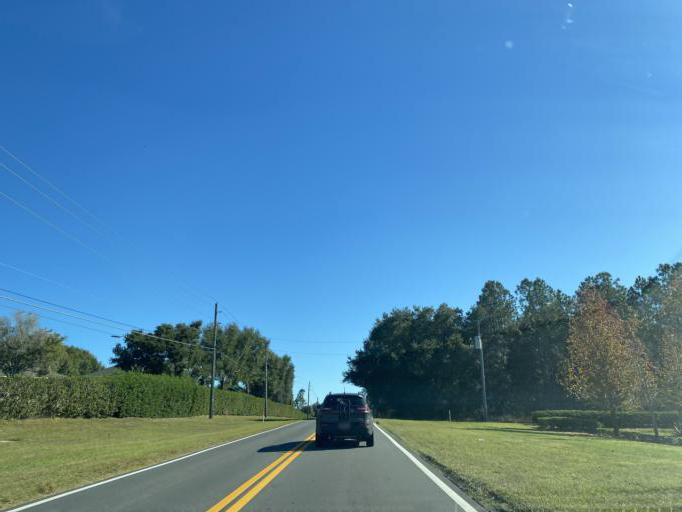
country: US
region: Florida
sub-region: Lake County
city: Clermont
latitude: 28.4998
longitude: -81.7117
